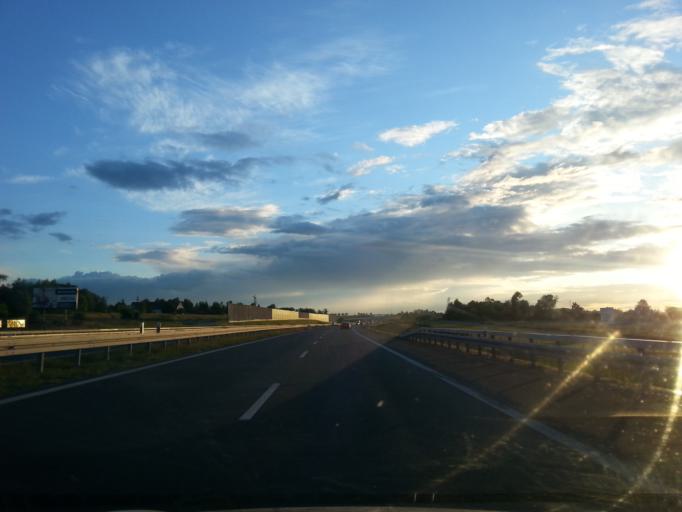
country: PL
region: Lower Silesian Voivodeship
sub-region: Powiat olesnicki
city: Sycow
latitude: 51.2938
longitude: 17.7135
